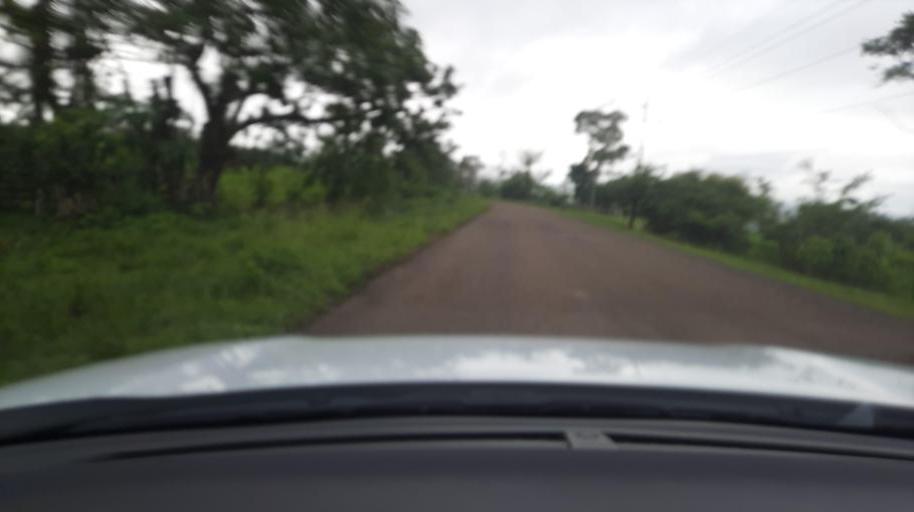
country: CR
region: Alajuela
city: San Jose
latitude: 11.0018
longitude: -85.2963
